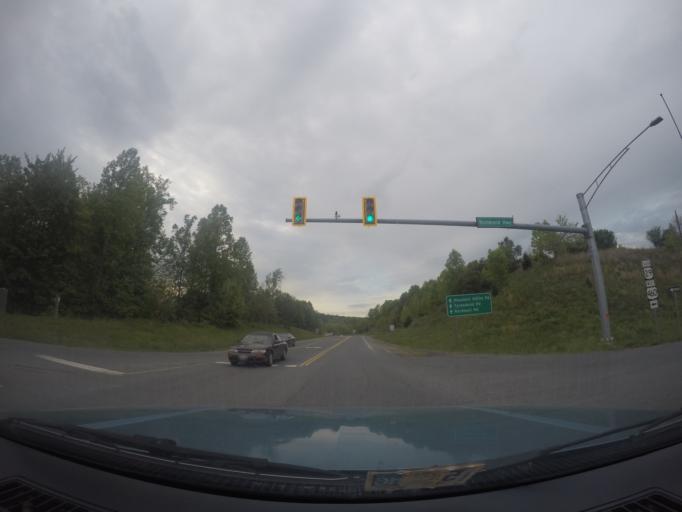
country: US
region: Virginia
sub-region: City of Lynchburg
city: Lynchburg
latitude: 37.3863
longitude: -79.1004
